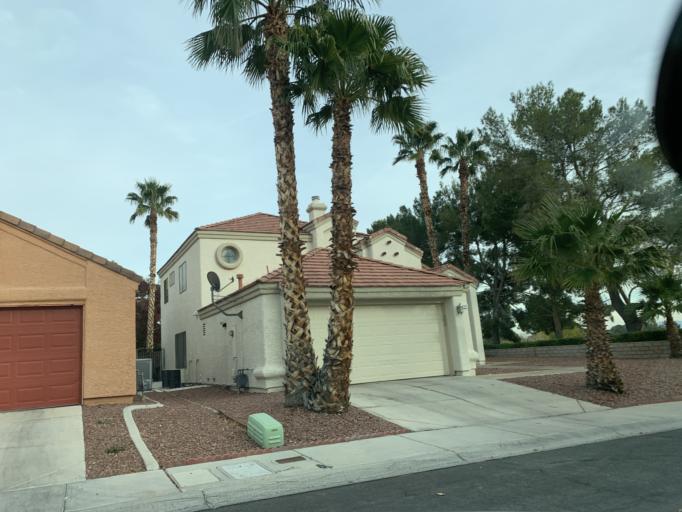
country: US
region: Nevada
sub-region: Clark County
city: Summerlin South
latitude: 36.1377
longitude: -115.2959
